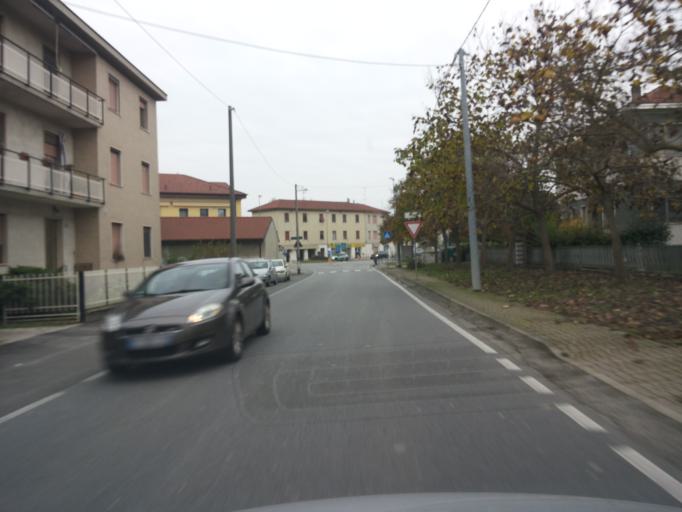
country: IT
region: Piedmont
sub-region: Provincia di Alessandria
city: Terruggia
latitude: 45.1008
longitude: 8.4519
